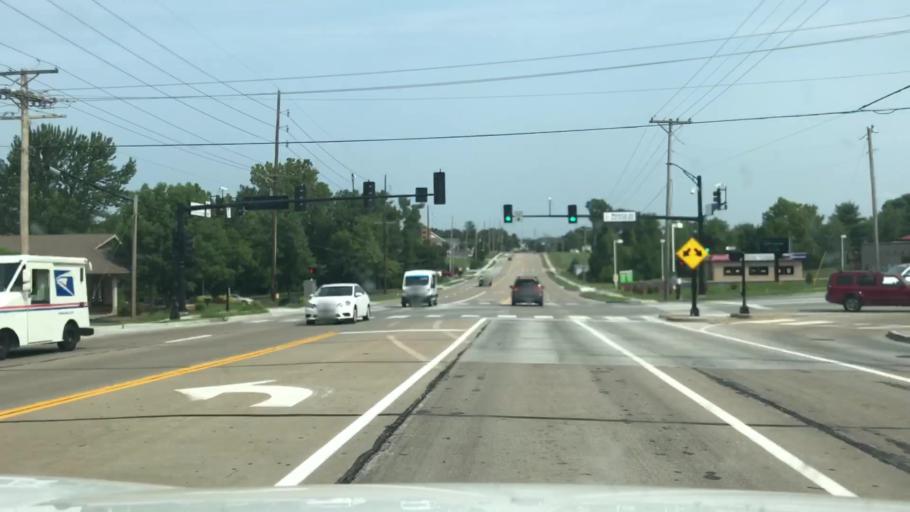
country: US
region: Missouri
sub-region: Saint Charles County
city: Dardenne Prairie
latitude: 38.7877
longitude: -90.7369
